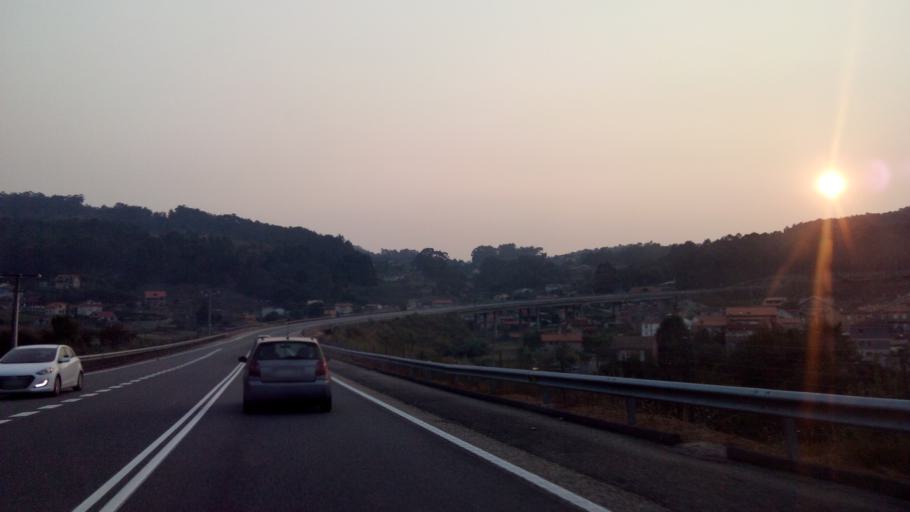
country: ES
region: Galicia
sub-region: Provincia de Pontevedra
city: Baiona
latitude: 42.1086
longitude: -8.8410
